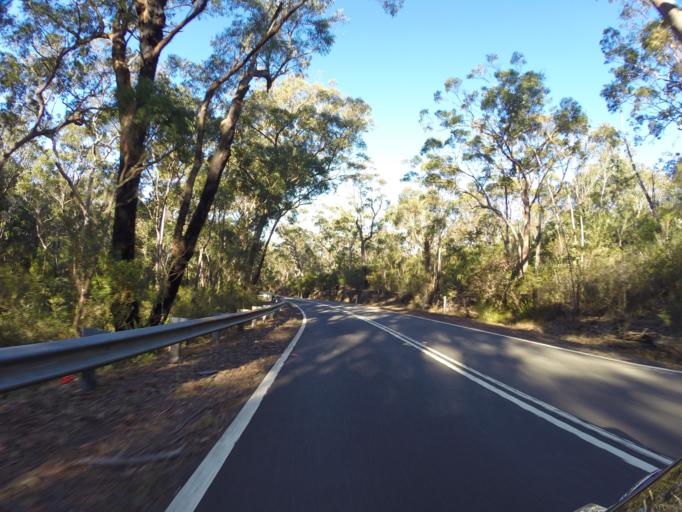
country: AU
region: New South Wales
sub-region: Wollongong
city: Helensburgh
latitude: -34.1446
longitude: 151.0008
